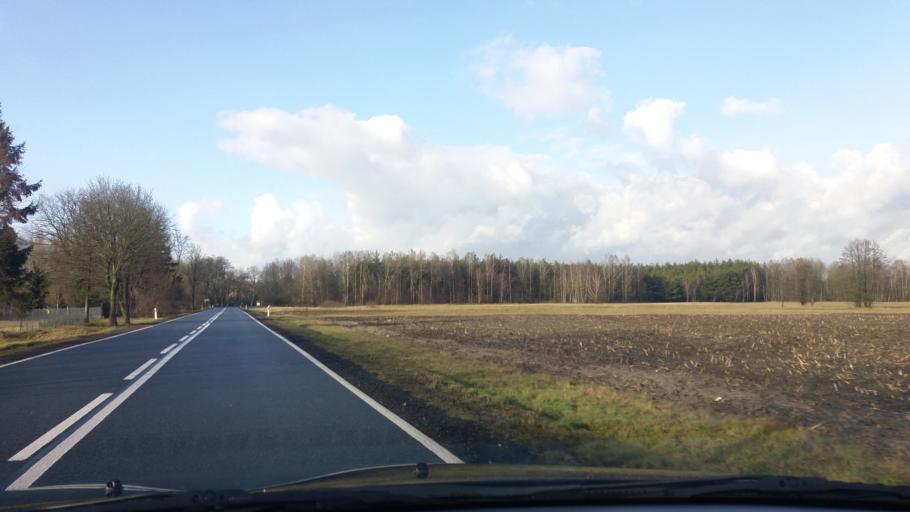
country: PL
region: Masovian Voivodeship
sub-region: Powiat przasnyski
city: Chorzele
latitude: 53.2771
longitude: 20.8993
